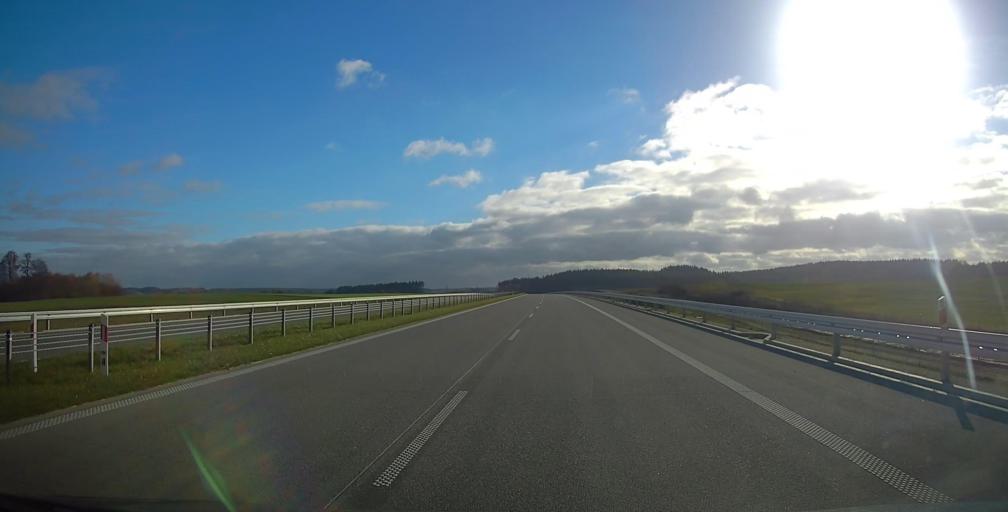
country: PL
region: Warmian-Masurian Voivodeship
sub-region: Powiat elcki
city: Elk
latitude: 53.7130
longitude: 22.2806
